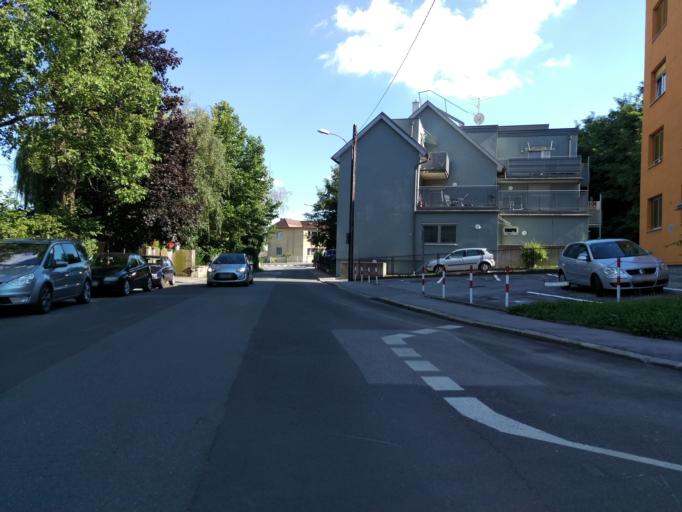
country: AT
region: Styria
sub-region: Graz Stadt
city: Wetzelsdorf
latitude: 47.0602
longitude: 15.3904
